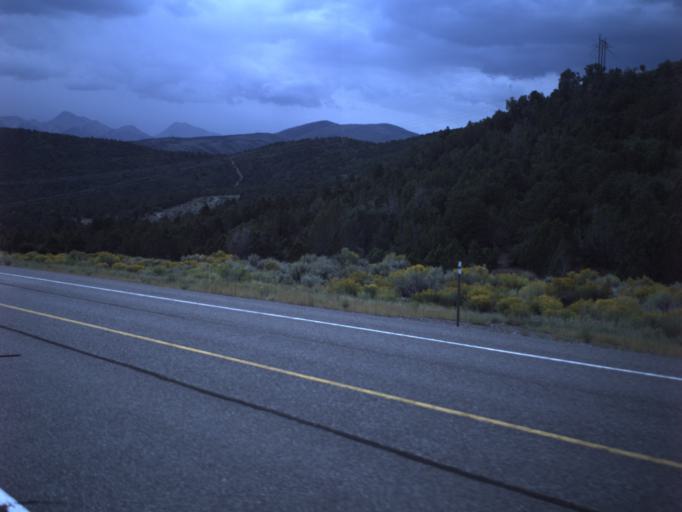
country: US
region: Utah
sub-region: Beaver County
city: Beaver
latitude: 38.5847
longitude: -112.4872
